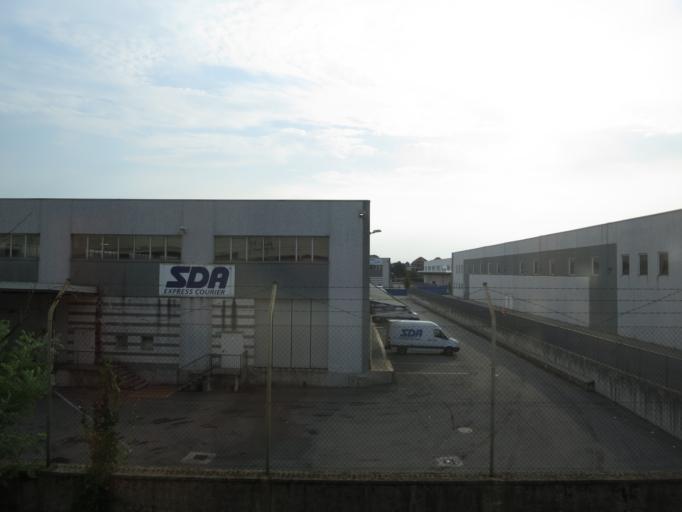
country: IT
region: Lombardy
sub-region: Provincia di Monza e Brianza
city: Desio
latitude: 45.6285
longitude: 9.2146
